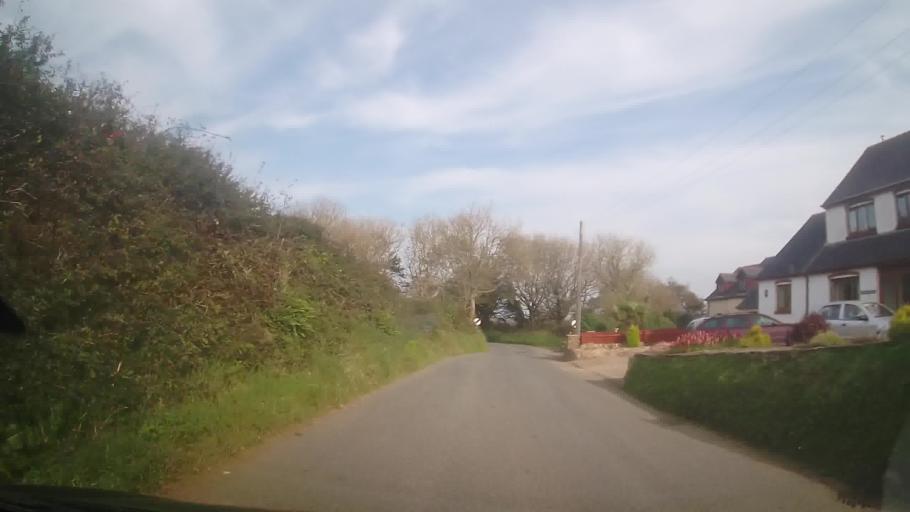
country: GB
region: Wales
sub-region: Pembrokeshire
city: Camrose
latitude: 51.8494
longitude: -5.0758
